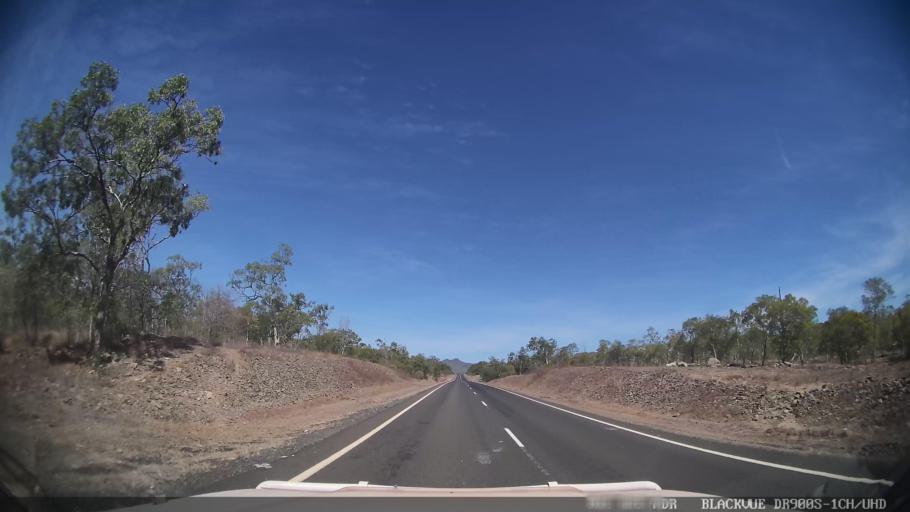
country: AU
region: Queensland
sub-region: Cook
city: Cooktown
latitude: -15.7007
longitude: 144.6062
